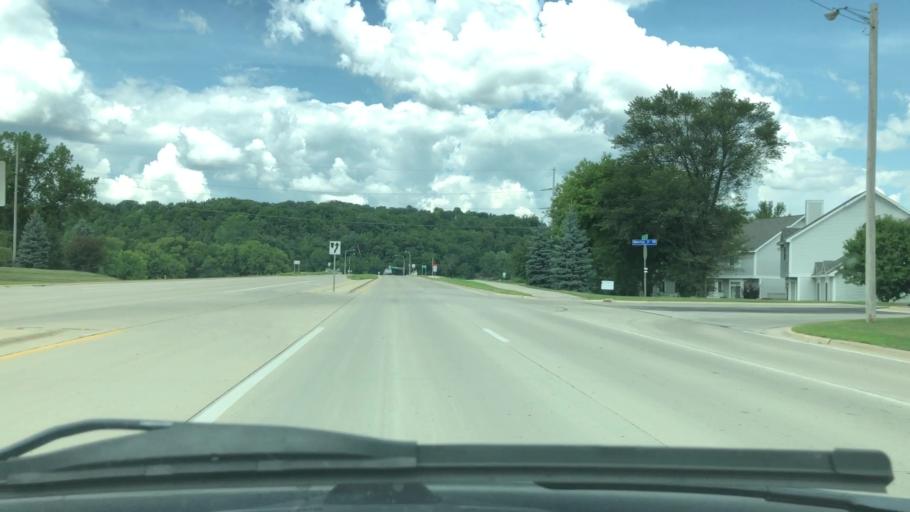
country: US
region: Minnesota
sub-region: Olmsted County
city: Rochester
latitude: 43.9952
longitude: -92.4984
